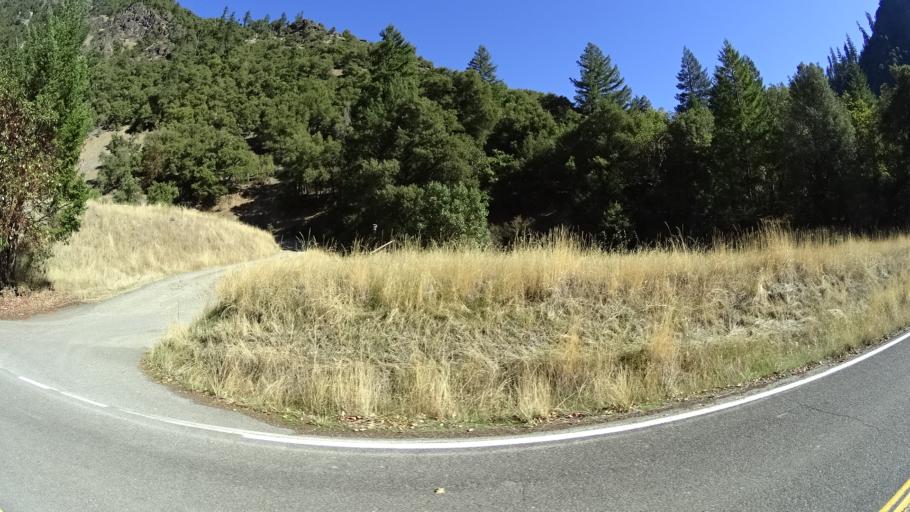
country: US
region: California
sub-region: Siskiyou County
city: Happy Camp
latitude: 41.3753
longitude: -123.4319
